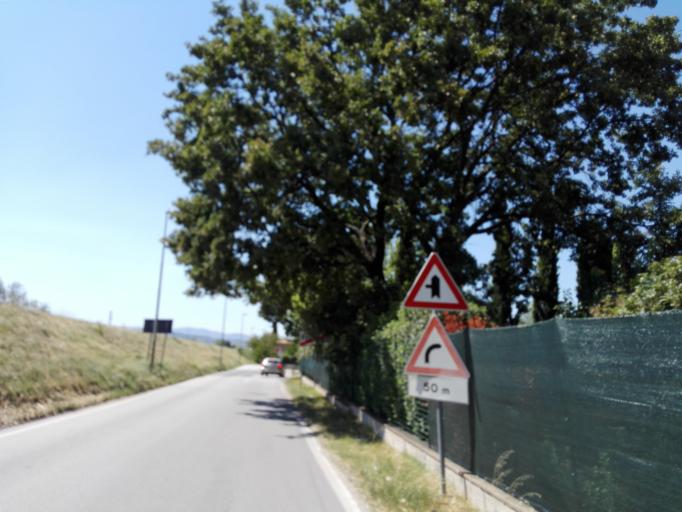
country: IT
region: Umbria
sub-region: Provincia di Perugia
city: Foligno
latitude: 42.9494
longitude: 12.6908
